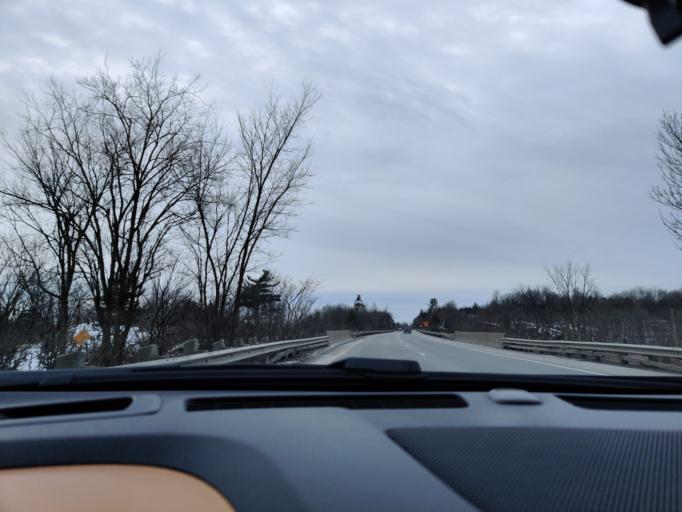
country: US
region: New York
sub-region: Jefferson County
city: Alexandria Bay
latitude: 44.4010
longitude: -75.9419
